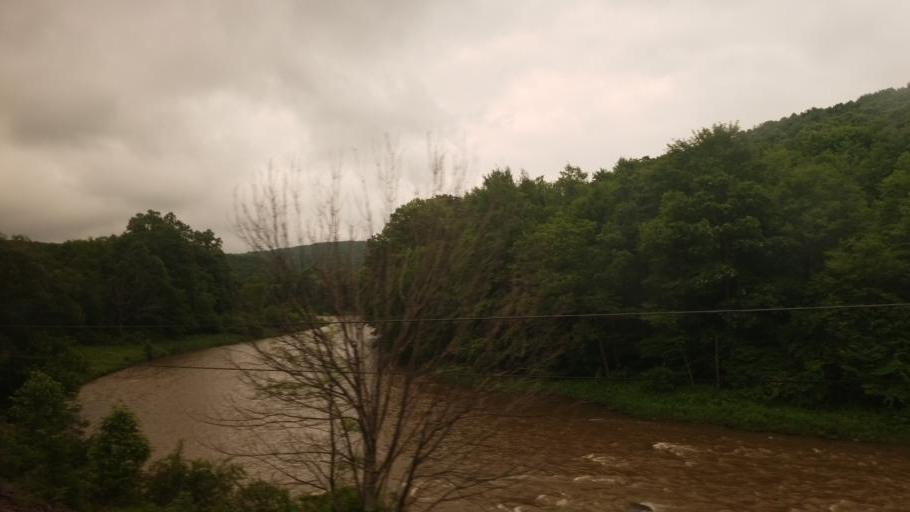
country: US
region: Pennsylvania
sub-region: Somerset County
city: Milford
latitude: 39.9058
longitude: -79.1367
